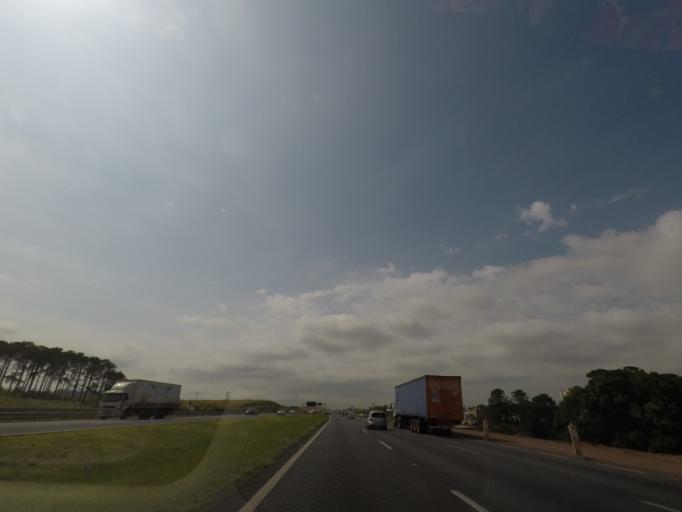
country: BR
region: Sao Paulo
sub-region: Campinas
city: Campinas
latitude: -22.8590
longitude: -47.0233
